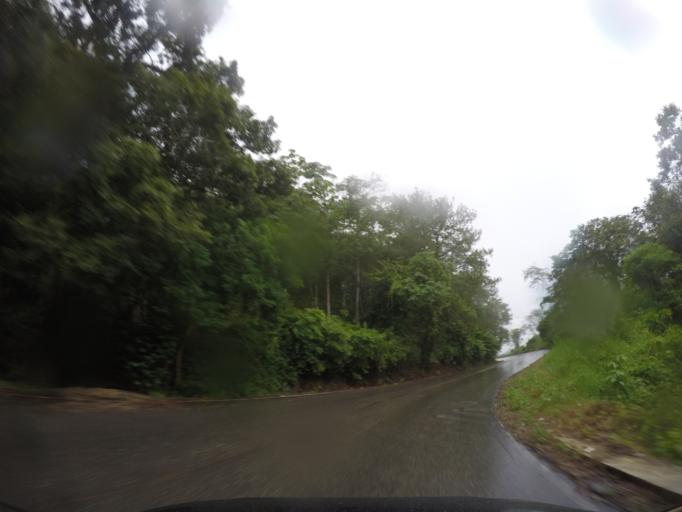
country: MX
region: Oaxaca
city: San Gabriel Mixtepec
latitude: 16.0808
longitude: -97.0810
